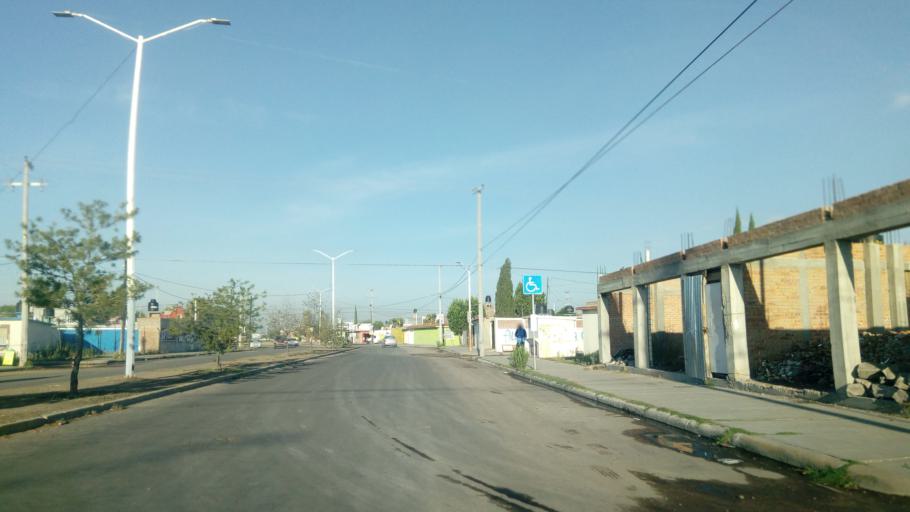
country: MX
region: Durango
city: Victoria de Durango
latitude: 24.0532
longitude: -104.5998
